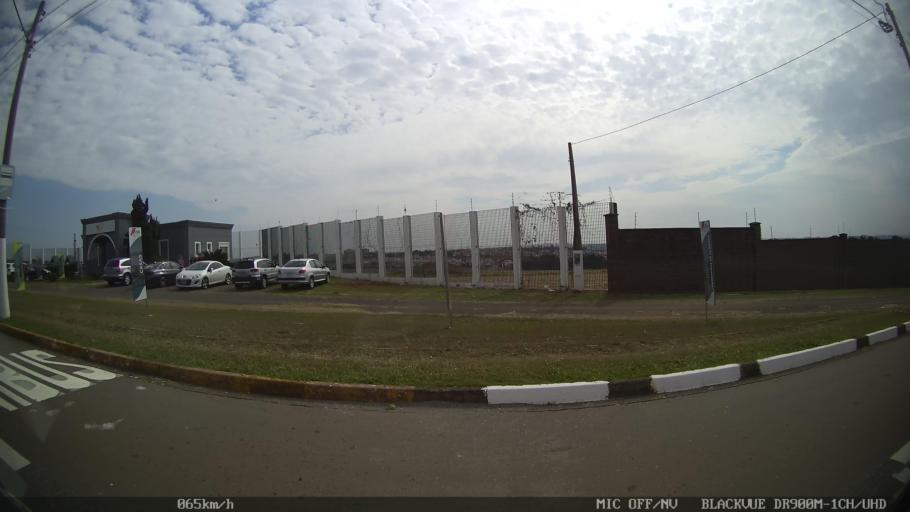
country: BR
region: Sao Paulo
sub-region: Paulinia
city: Paulinia
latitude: -22.7871
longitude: -47.1654
